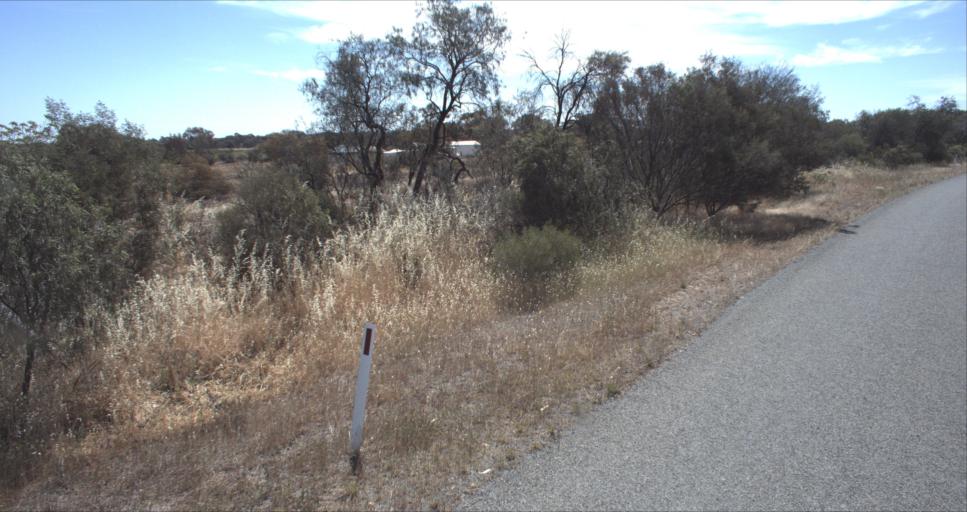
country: AU
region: New South Wales
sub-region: Leeton
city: Leeton
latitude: -34.5838
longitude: 146.4294
